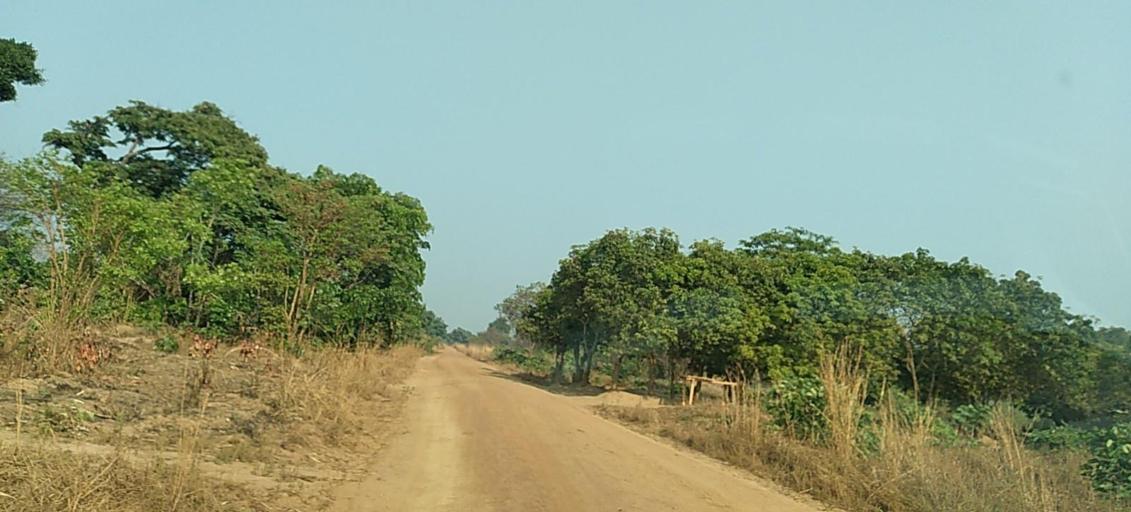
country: ZM
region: Copperbelt
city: Chingola
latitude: -12.8574
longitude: 27.5643
